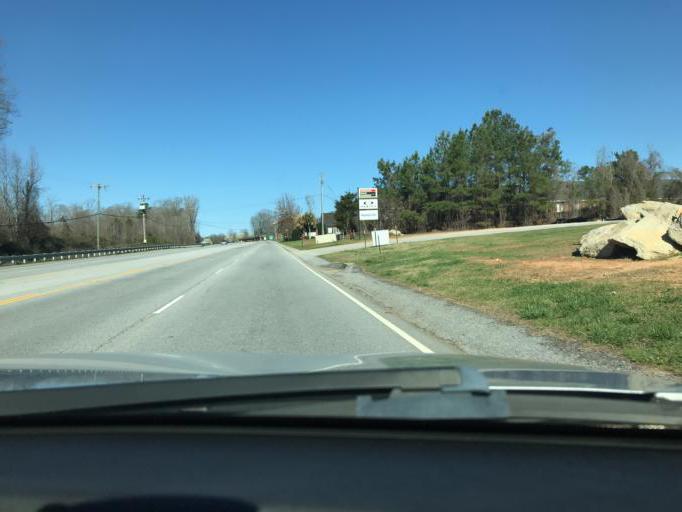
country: US
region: South Carolina
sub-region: Laurens County
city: Clinton
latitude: 34.4763
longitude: -81.9342
